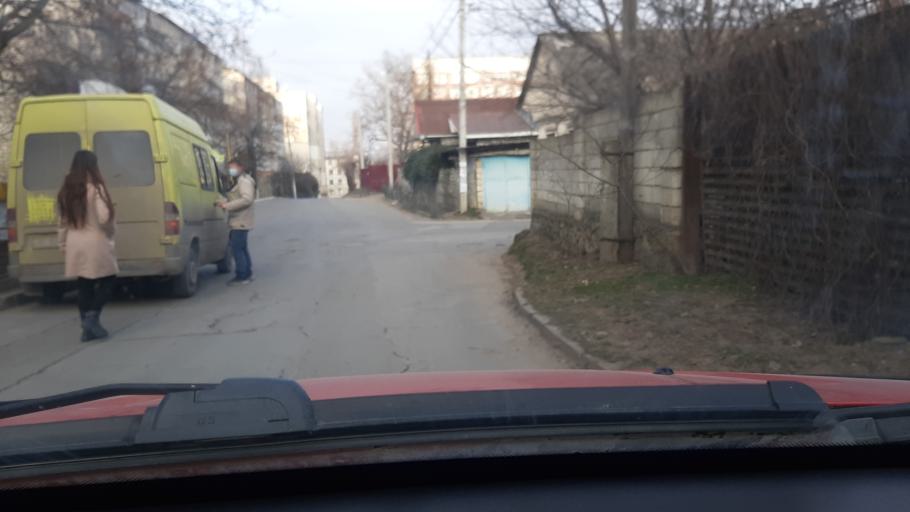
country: MD
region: Chisinau
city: Vatra
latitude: 47.0412
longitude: 28.7903
